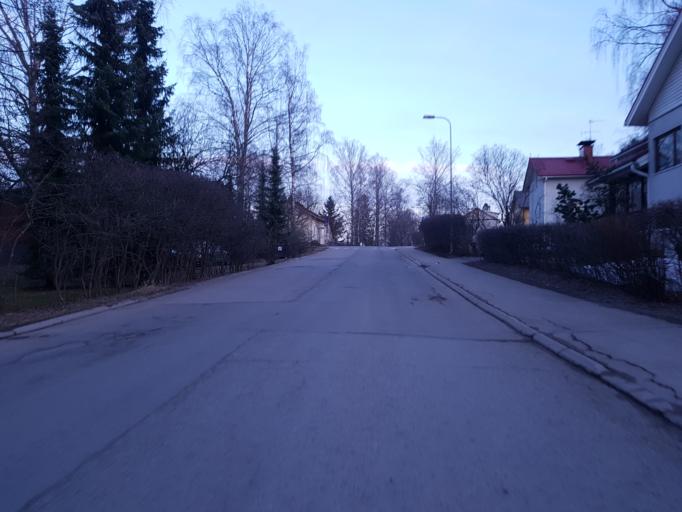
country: FI
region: Uusimaa
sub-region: Helsinki
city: Helsinki
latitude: 60.2616
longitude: 24.9516
